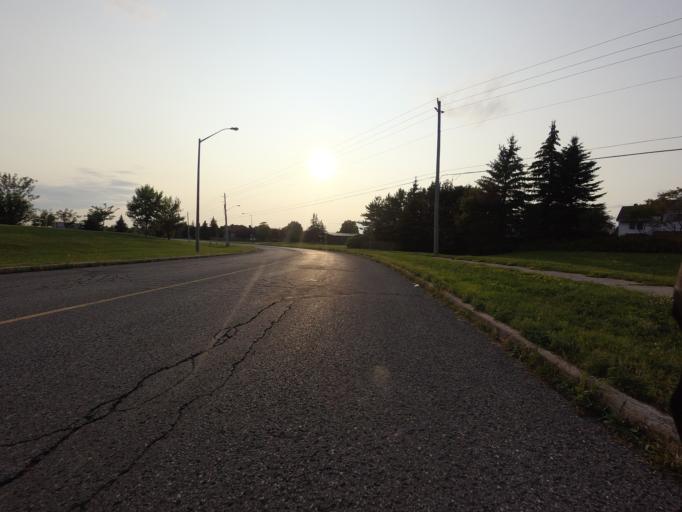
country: CA
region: Ontario
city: Bells Corners
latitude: 45.3257
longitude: -75.7723
